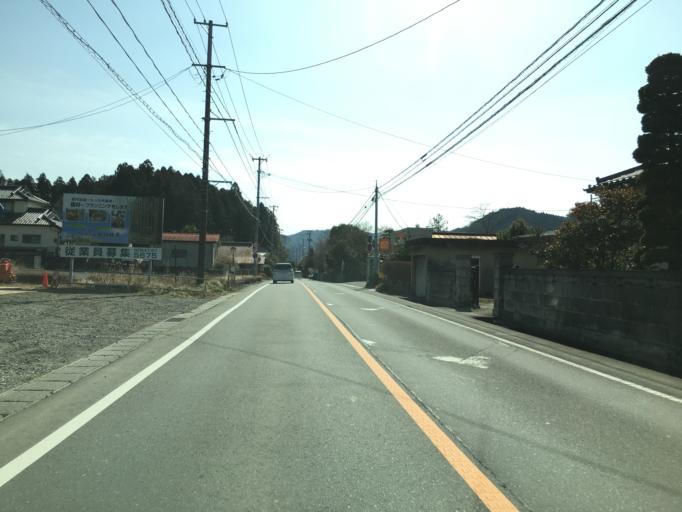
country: JP
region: Ibaraki
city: Daigo
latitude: 36.8844
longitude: 140.4202
